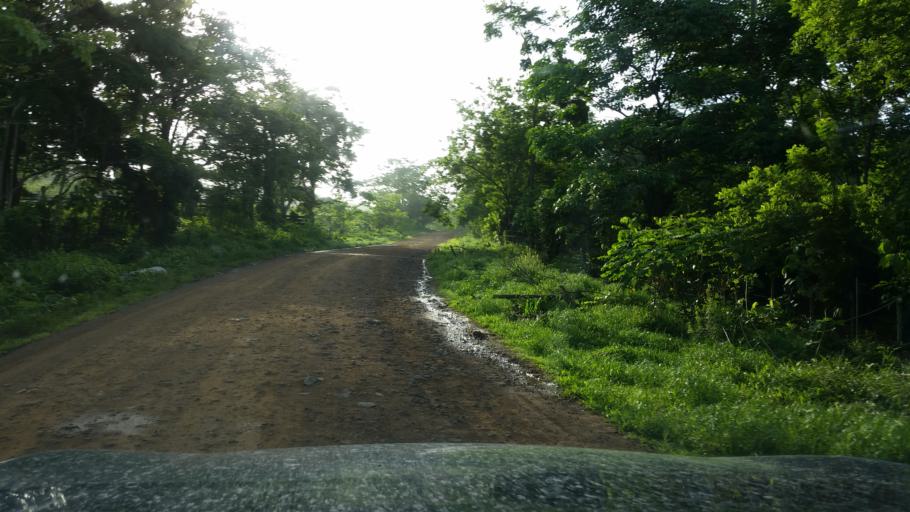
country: NI
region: Atlantico Norte (RAAN)
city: Puerto Cabezas
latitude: 14.0683
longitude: -83.9779
